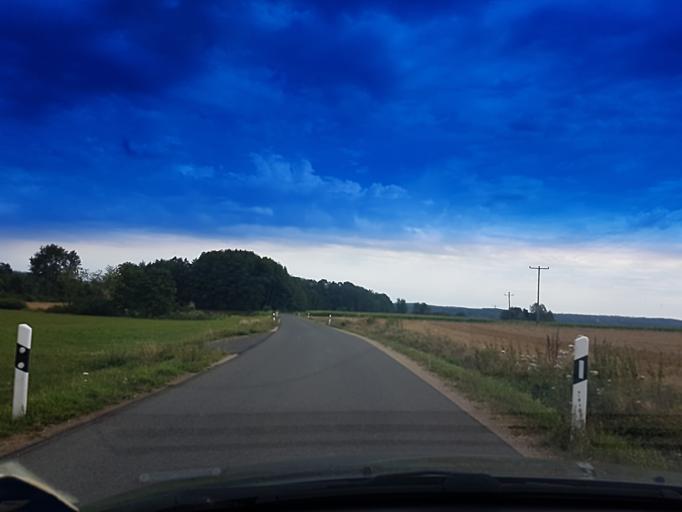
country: DE
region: Bavaria
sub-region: Upper Franconia
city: Frensdorf
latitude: 49.8318
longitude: 10.8620
